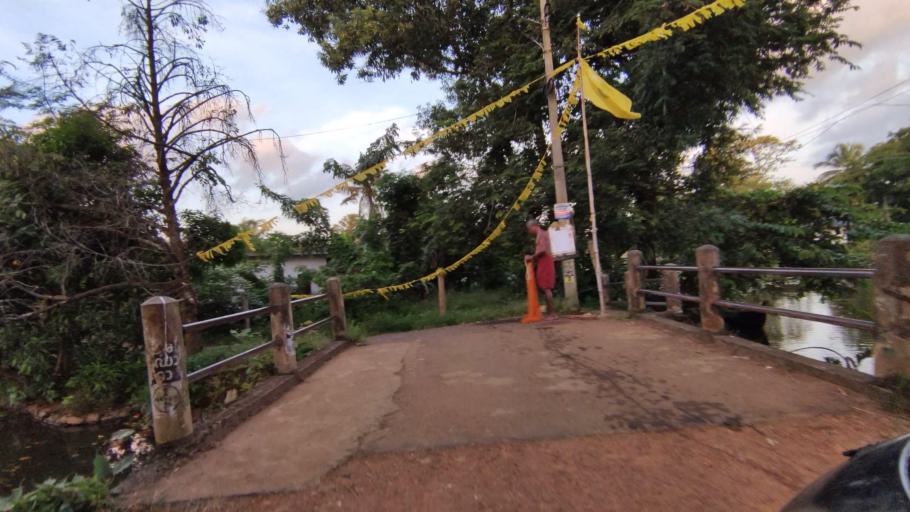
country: IN
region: Kerala
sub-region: Kottayam
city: Kottayam
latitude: 9.5757
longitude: 76.4521
